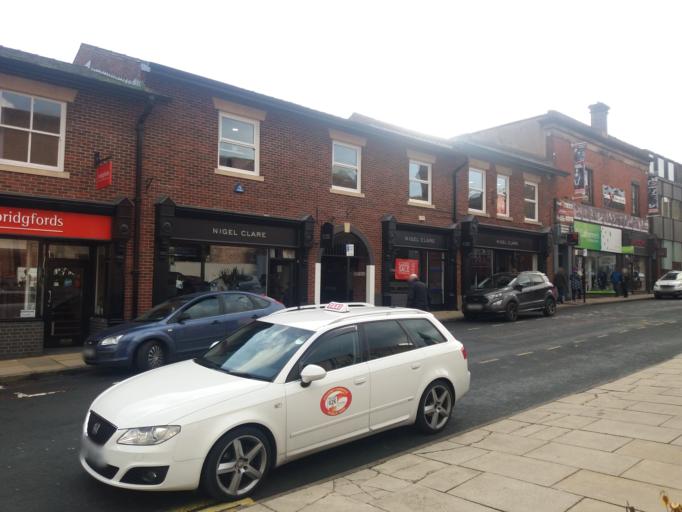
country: GB
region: England
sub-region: Lancashire
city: Chorley
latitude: 53.6538
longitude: -2.6316
